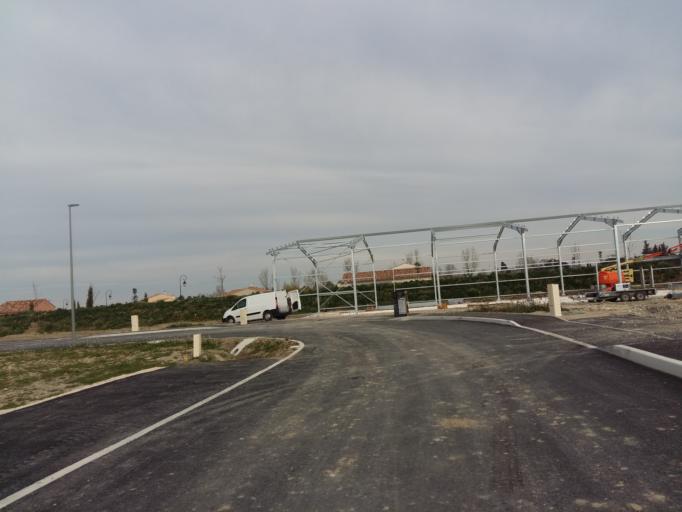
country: FR
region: Provence-Alpes-Cote d'Azur
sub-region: Departement du Vaucluse
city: Le Thor
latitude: 43.9244
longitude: 5.0138
